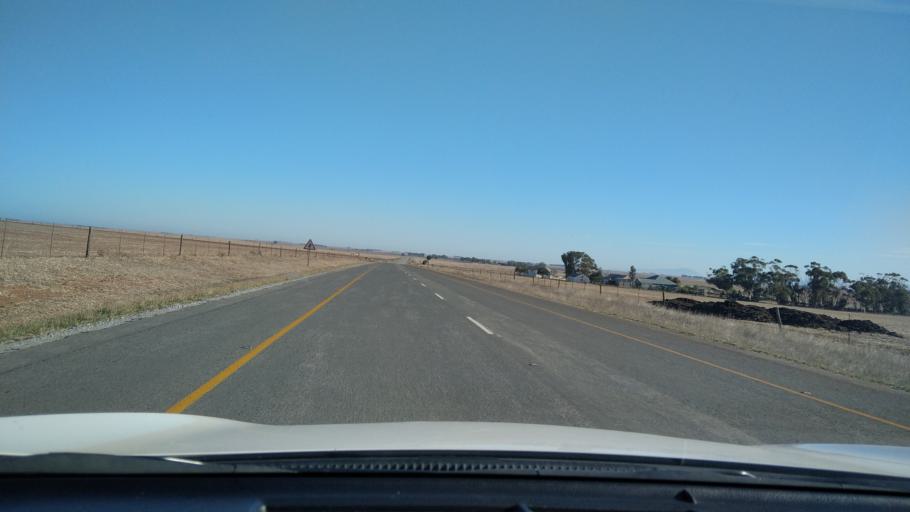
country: ZA
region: Western Cape
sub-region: West Coast District Municipality
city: Moorreesburg
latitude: -33.3070
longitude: 18.6176
